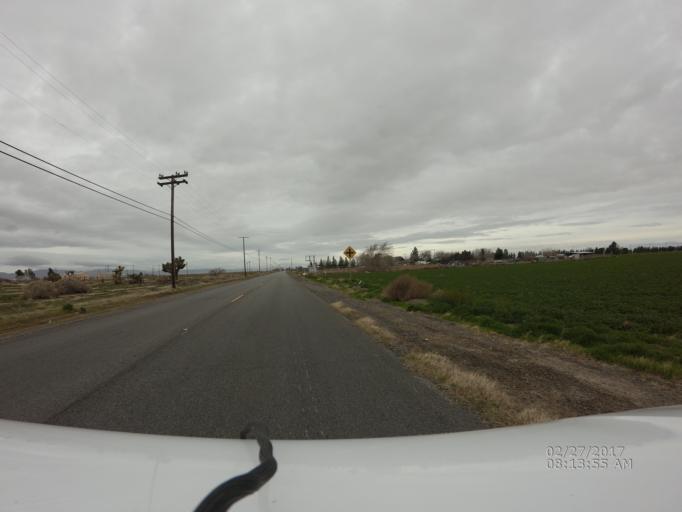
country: US
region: California
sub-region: Los Angeles County
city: Lancaster
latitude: 34.7047
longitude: -118.0030
